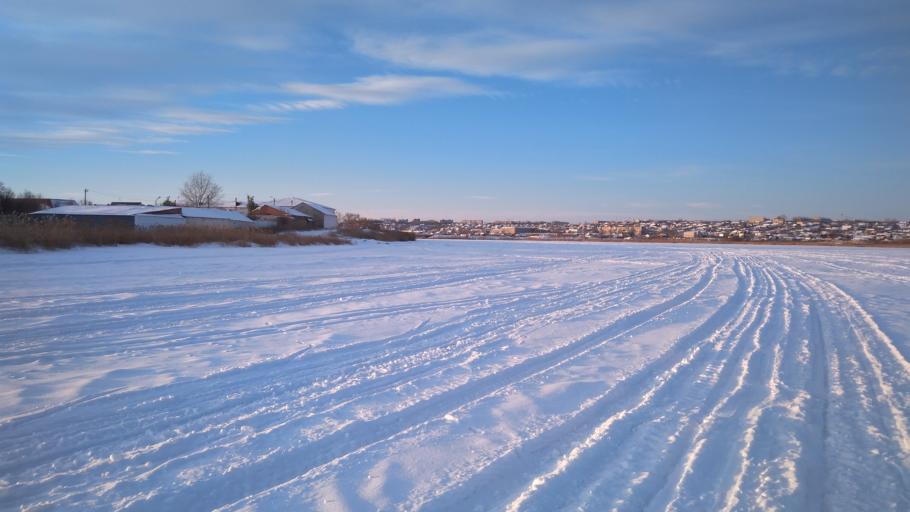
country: RU
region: Chelyabinsk
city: Troitsk
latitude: 54.0864
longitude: 61.5861
